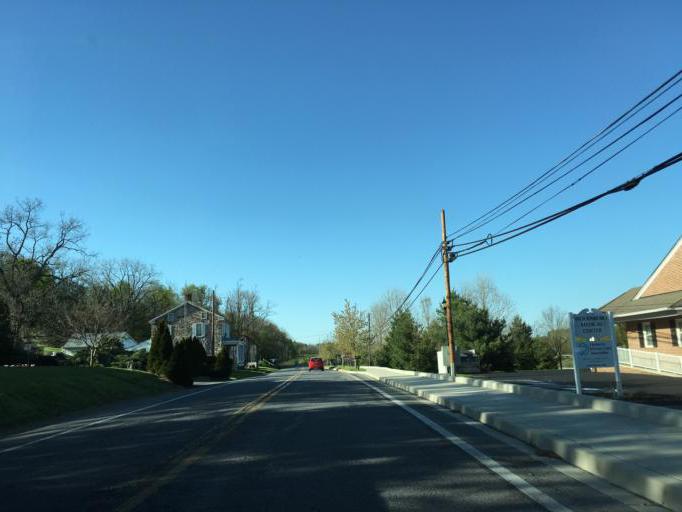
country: US
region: Maryland
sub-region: Frederick County
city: Woodsboro
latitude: 39.5380
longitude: -77.3145
